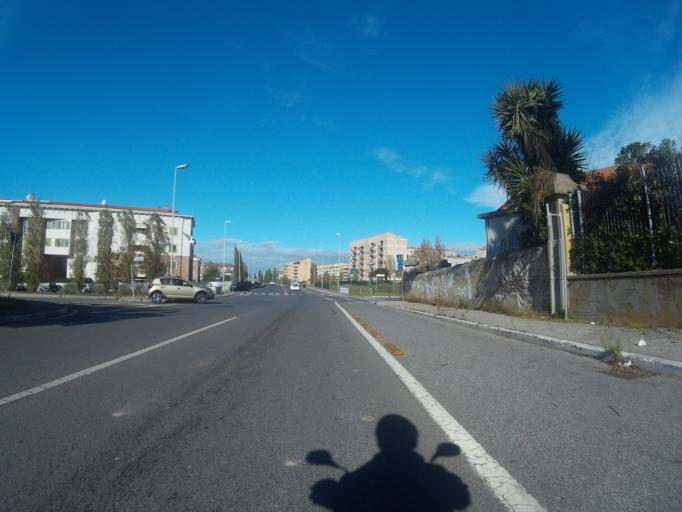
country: IT
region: Tuscany
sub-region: Provincia di Livorno
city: Livorno
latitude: 43.5245
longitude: 10.3459
